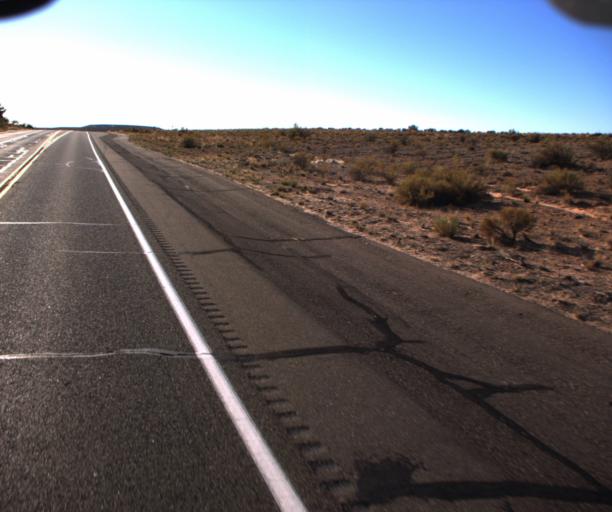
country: US
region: Arizona
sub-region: Coconino County
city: Page
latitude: 36.9927
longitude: -111.5630
